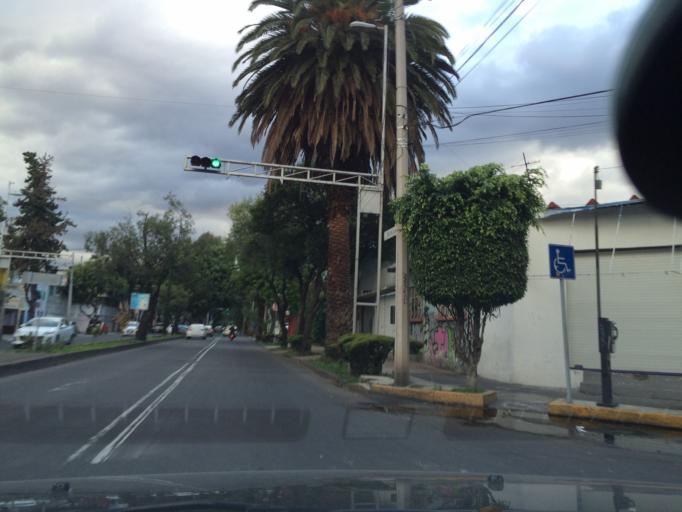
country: MX
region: Mexico City
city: Colonia Nativitas
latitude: 19.3654
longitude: -99.1490
